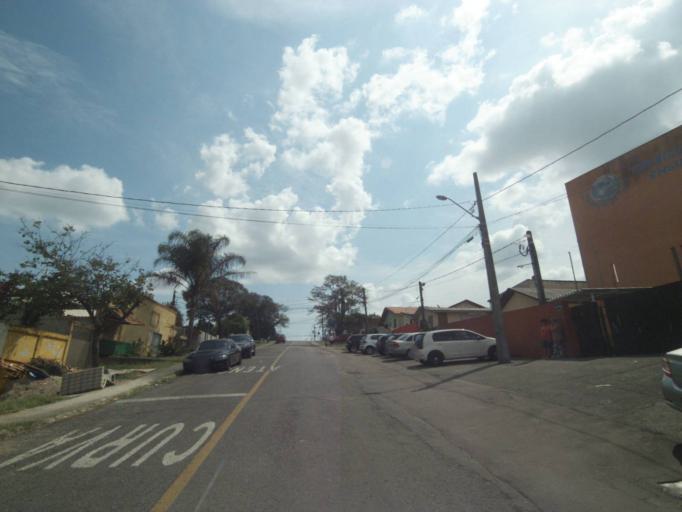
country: BR
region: Parana
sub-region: Pinhais
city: Pinhais
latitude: -25.3978
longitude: -49.1966
